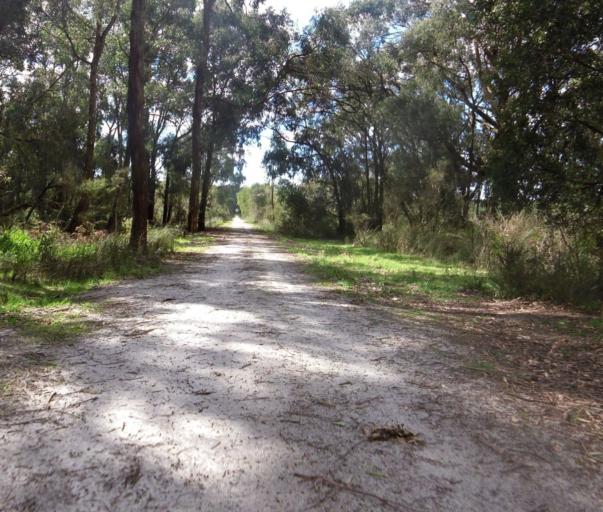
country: AU
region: Victoria
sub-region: Bass Coast
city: North Wonthaggi
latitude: -38.6141
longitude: 146.0430
